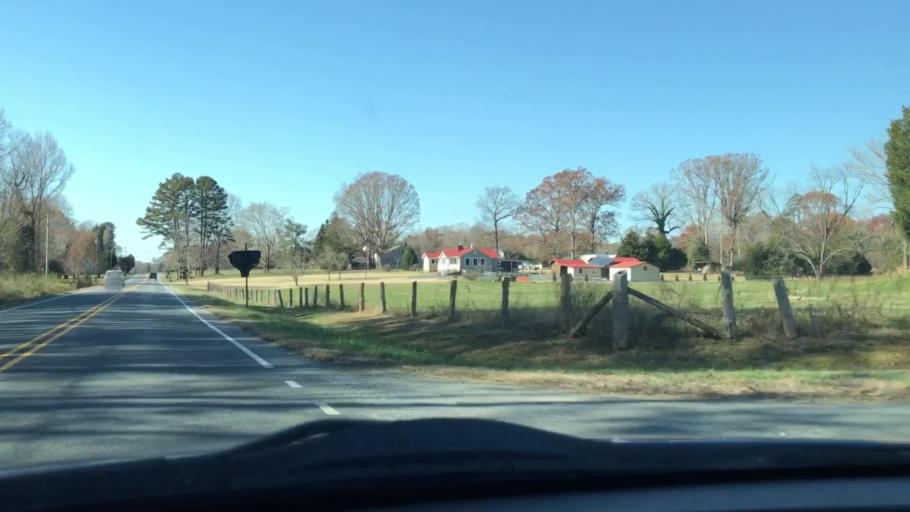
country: US
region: North Carolina
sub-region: Randolph County
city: Asheboro
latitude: 35.6734
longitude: -79.9198
